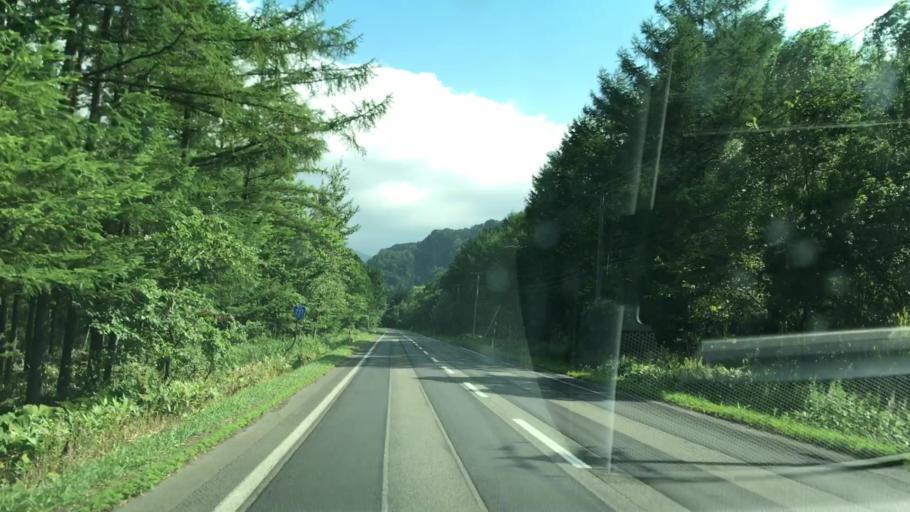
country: JP
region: Hokkaido
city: Shizunai-furukawacho
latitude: 42.8292
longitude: 142.4161
